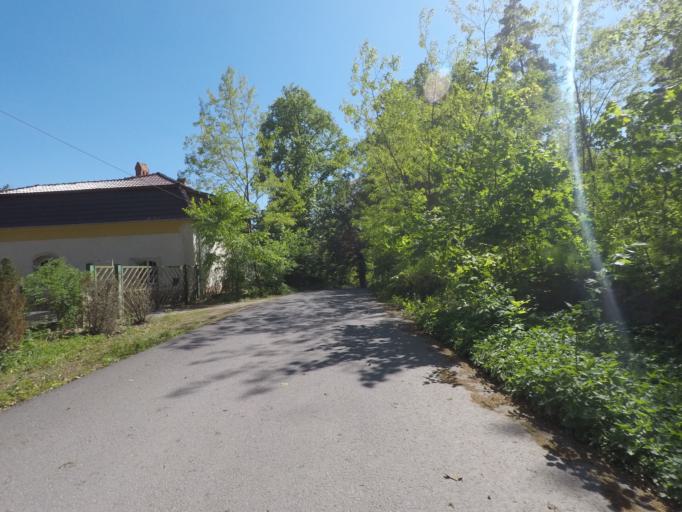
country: DE
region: Brandenburg
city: Eberswalde
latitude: 52.8131
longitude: 13.7776
